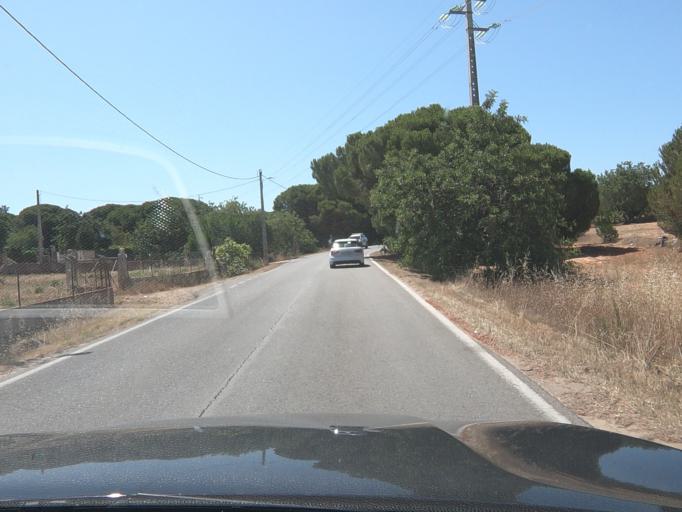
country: PT
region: Faro
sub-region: Loule
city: Vilamoura
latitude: 37.0998
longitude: -8.0969
